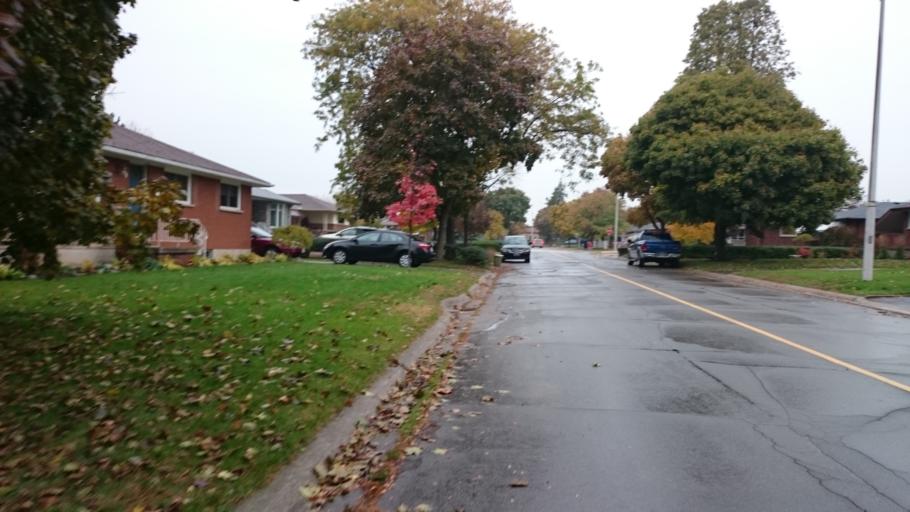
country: CA
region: Ontario
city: Brantford
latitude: 43.1695
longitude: -80.2874
